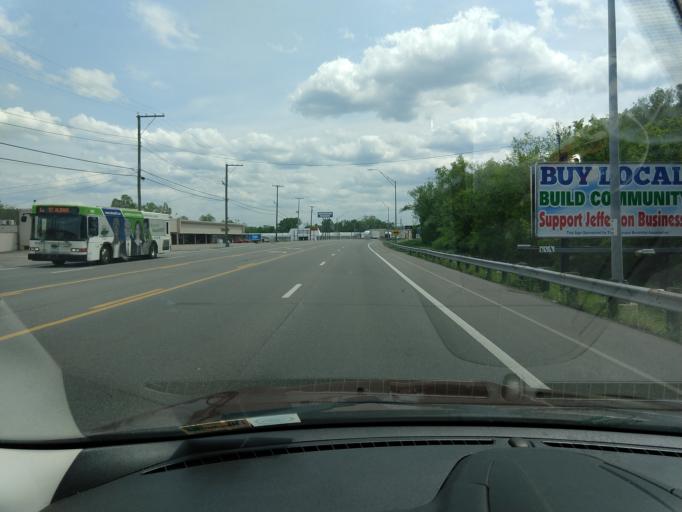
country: US
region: West Virginia
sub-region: Kanawha County
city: Dunbar
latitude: 38.3703
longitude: -81.7685
